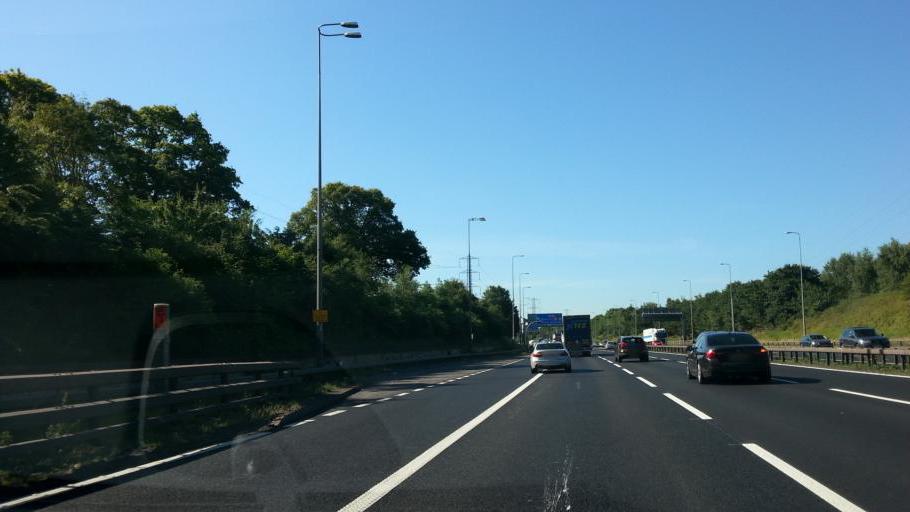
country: GB
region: England
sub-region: Solihull
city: Bickenhill
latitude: 52.4602
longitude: -1.7103
